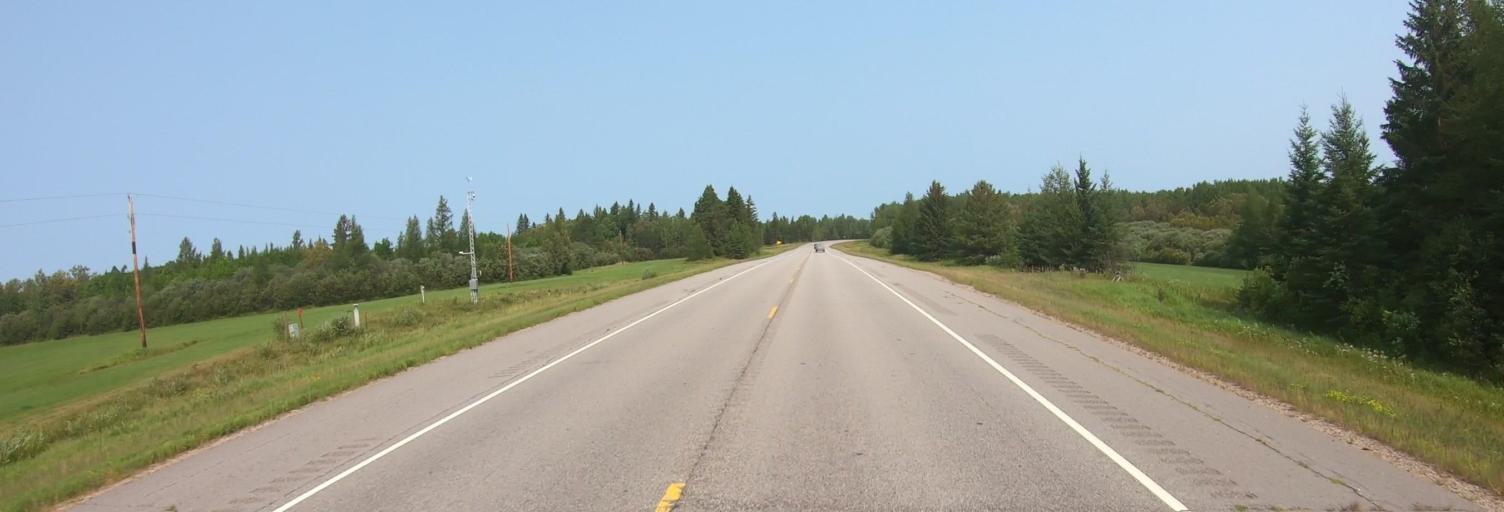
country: CA
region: Ontario
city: Fort Frances
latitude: 48.2938
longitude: -92.9700
